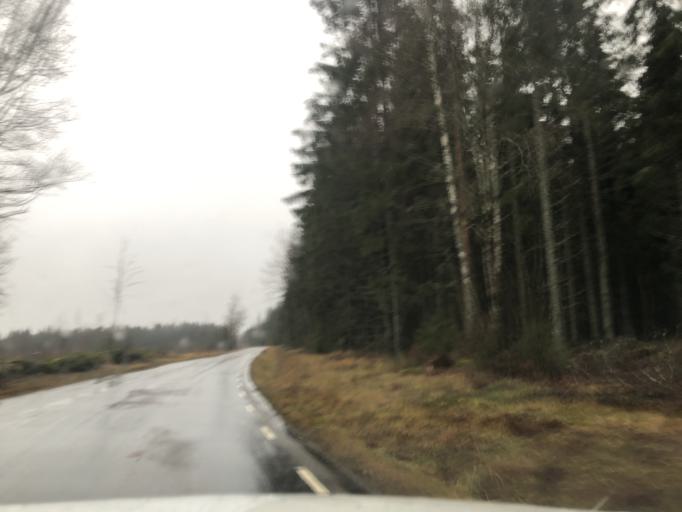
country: SE
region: Vaestra Goetaland
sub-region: Ulricehamns Kommun
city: Ulricehamn
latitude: 57.8421
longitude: 13.5390
